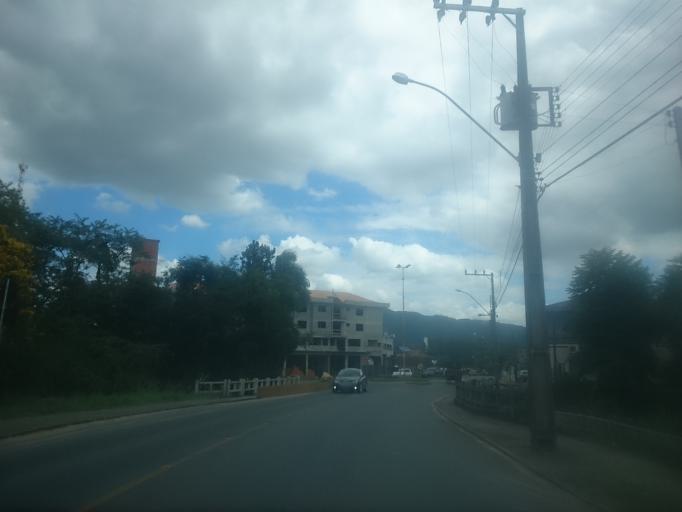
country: BR
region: Santa Catarina
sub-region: Pomerode
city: Pomerode
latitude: -26.7125
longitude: -49.1645
